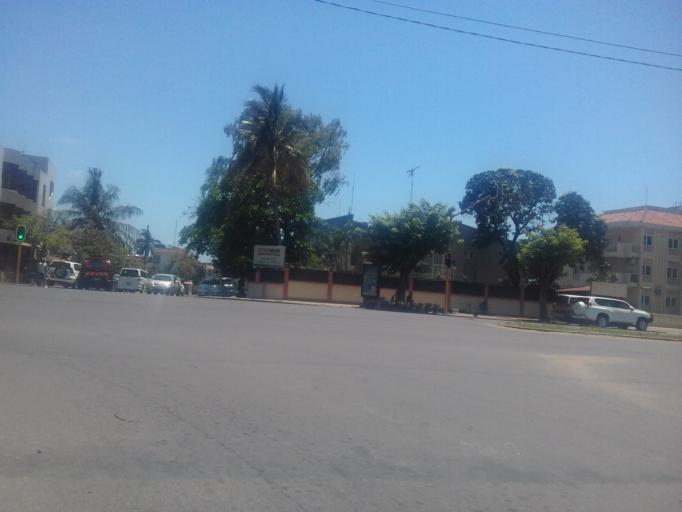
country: MZ
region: Maputo City
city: Maputo
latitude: -25.9542
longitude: 32.5909
